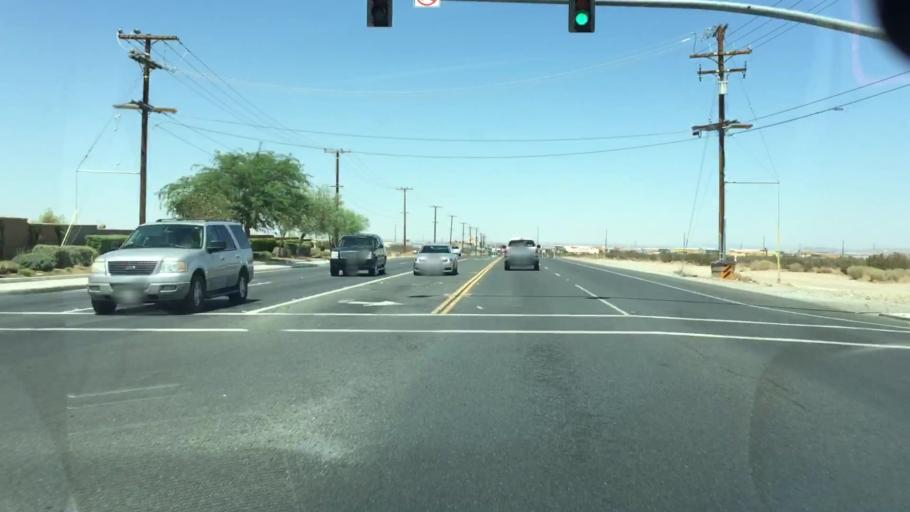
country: US
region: California
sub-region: San Bernardino County
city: Mountain View Acres
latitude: 34.4997
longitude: -117.3995
